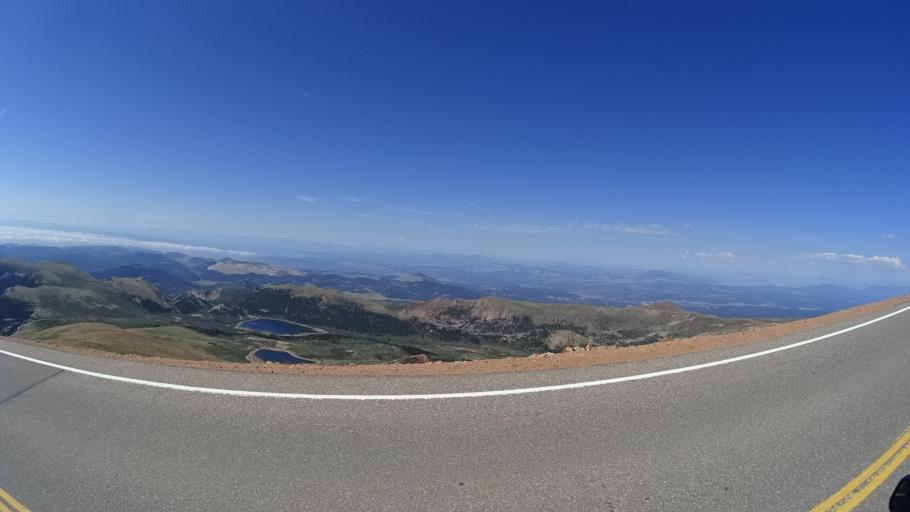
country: US
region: Colorado
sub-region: El Paso County
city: Cascade-Chipita Park
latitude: 38.8391
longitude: -105.0452
